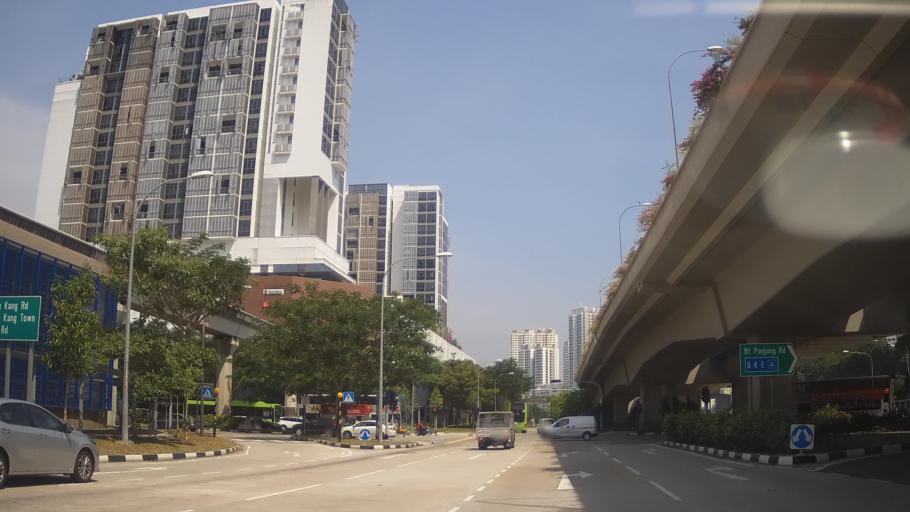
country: MY
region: Johor
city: Johor Bahru
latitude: 1.3790
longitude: 103.7614
